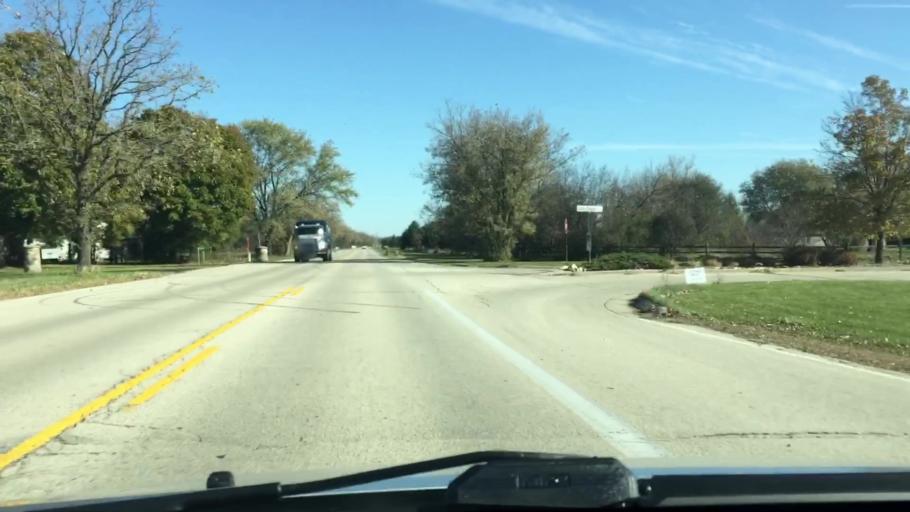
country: US
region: Wisconsin
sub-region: Waukesha County
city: North Prairie
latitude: 42.9682
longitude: -88.4036
